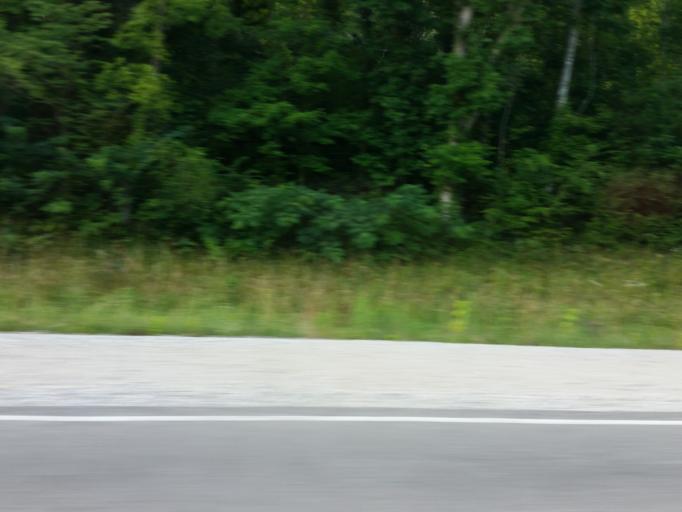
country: US
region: Tennessee
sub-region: Lewis County
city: Hohenwald
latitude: 35.5636
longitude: -87.3806
